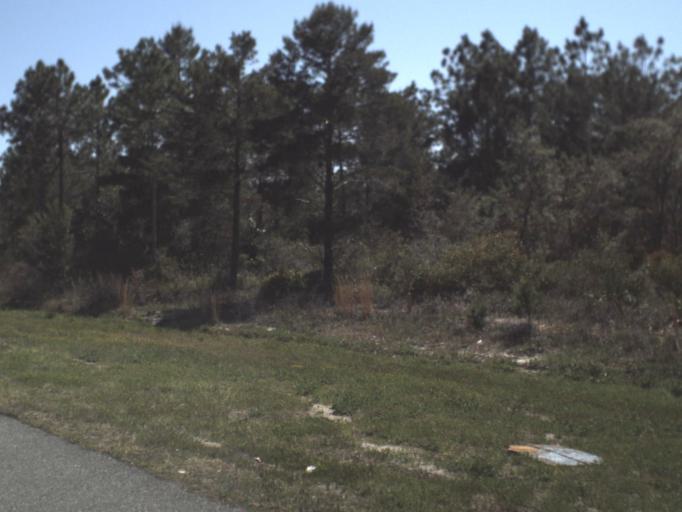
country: US
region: Florida
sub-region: Gulf County
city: Port Saint Joe
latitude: 29.8821
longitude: -85.3428
